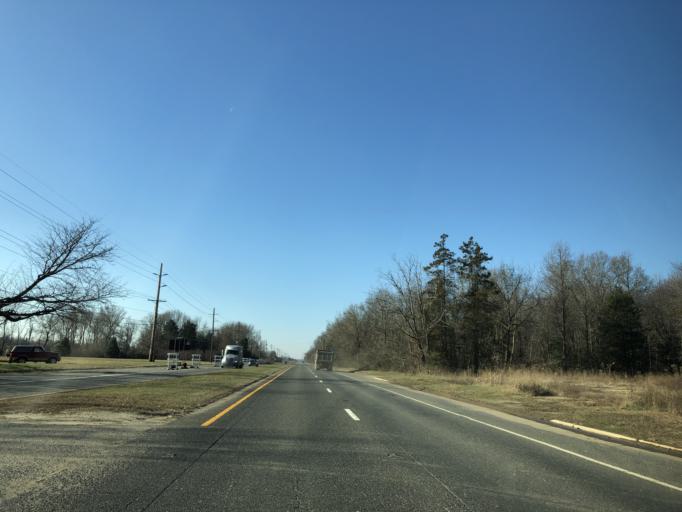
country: US
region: New Jersey
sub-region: Gloucester County
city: Beckett
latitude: 39.7941
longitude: -75.3723
